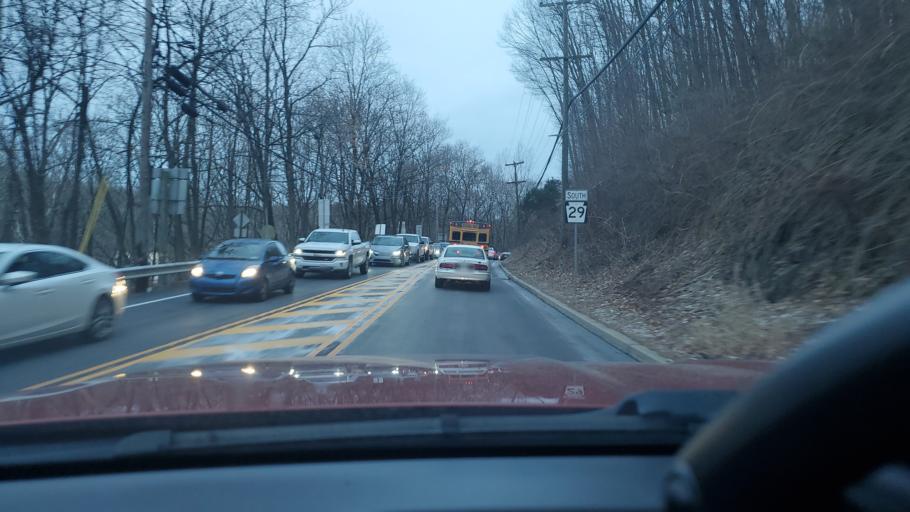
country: US
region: Pennsylvania
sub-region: Montgomery County
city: Schwenksville
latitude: 40.2511
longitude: -75.4609
